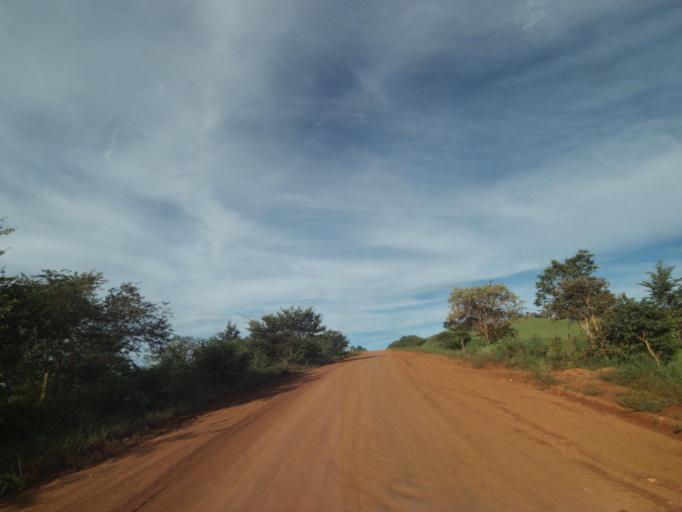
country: BR
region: Goias
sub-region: Jaragua
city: Jaragua
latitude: -15.8976
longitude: -49.5247
